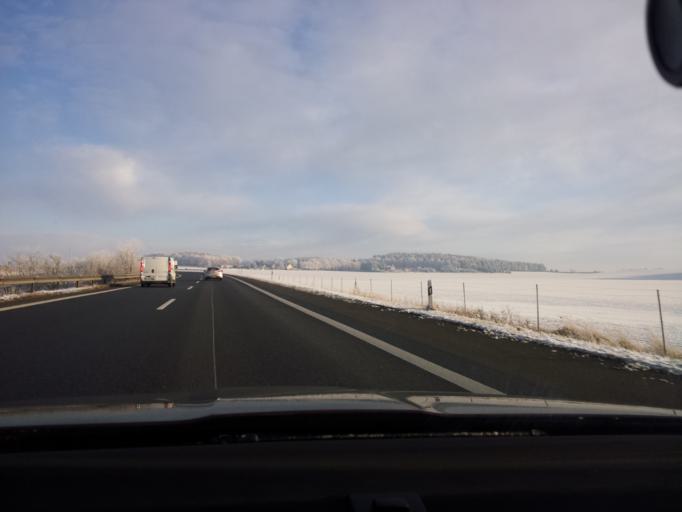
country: DE
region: Brandenburg
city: Wittstock
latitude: 53.1271
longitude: 12.4637
